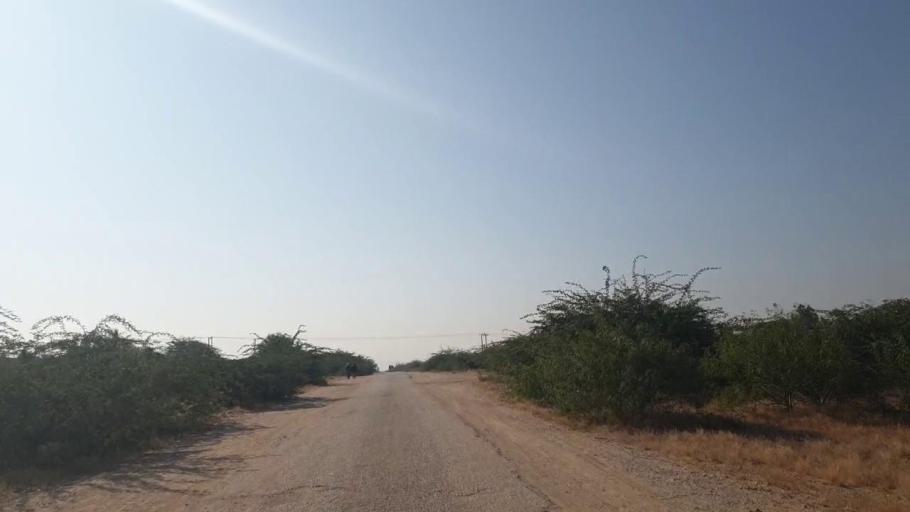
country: PK
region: Sindh
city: Thatta
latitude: 25.1522
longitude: 67.7740
